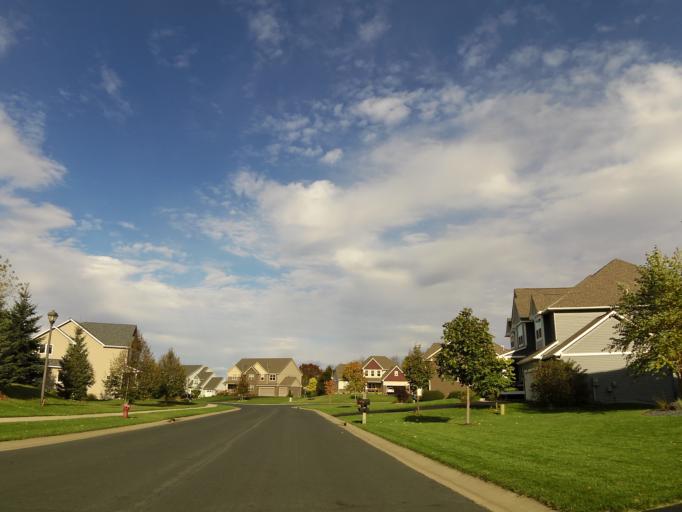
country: US
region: Minnesota
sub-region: Scott County
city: Prior Lake
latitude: 44.6993
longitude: -93.4447
